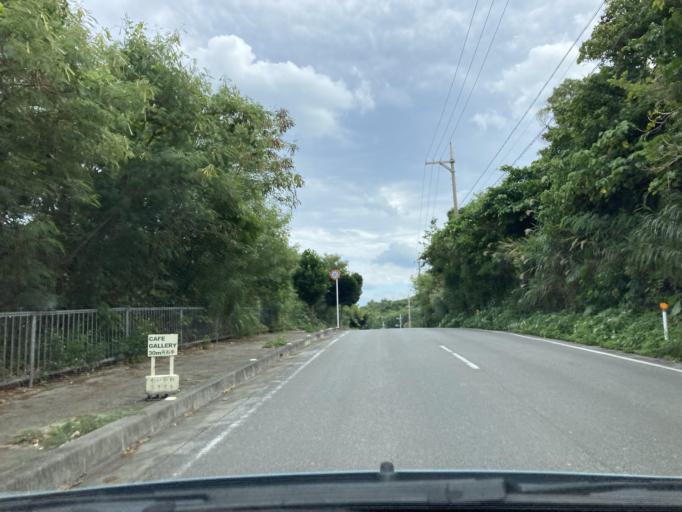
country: JP
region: Okinawa
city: Katsuren-haebaru
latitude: 26.3263
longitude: 127.9598
